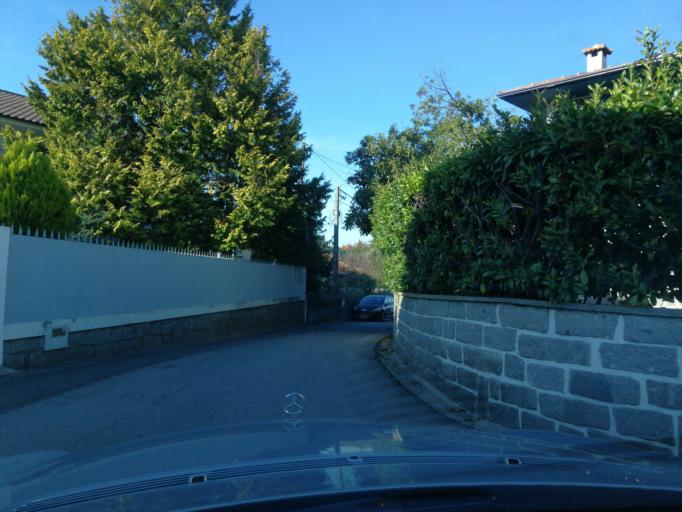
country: PT
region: Braga
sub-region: Vila Nova de Famalicao
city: Vila Nova de Famalicao
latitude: 41.4261
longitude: -8.5192
